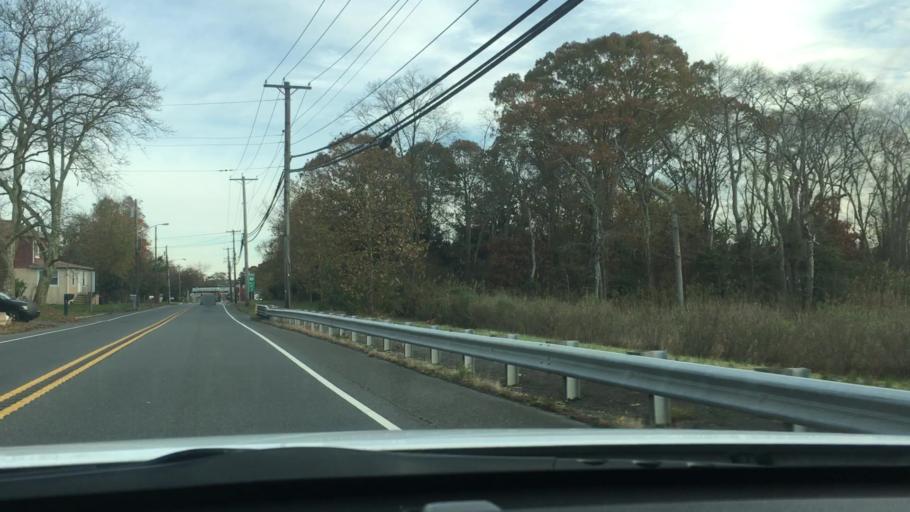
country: US
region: New Jersey
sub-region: Atlantic County
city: Absecon
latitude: 39.4238
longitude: -74.5076
